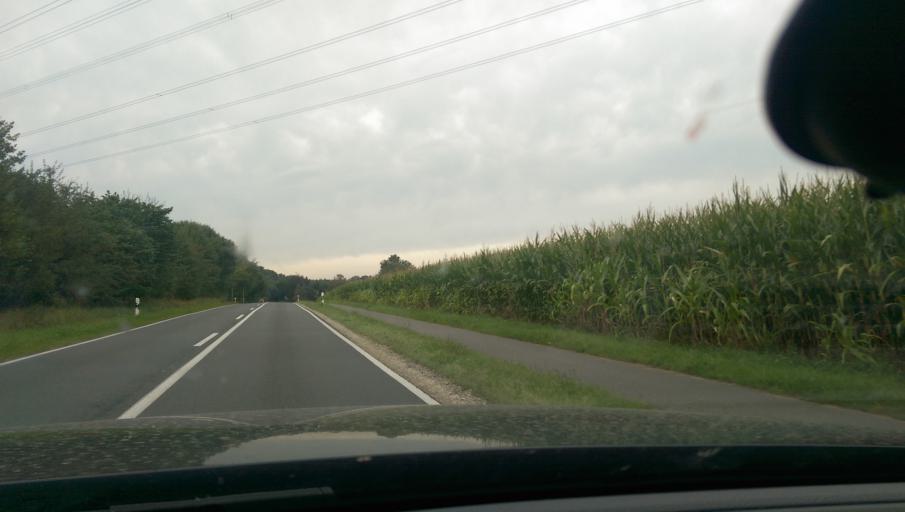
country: DE
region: Lower Saxony
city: Rehburg-Loccum
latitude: 52.4638
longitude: 9.1743
